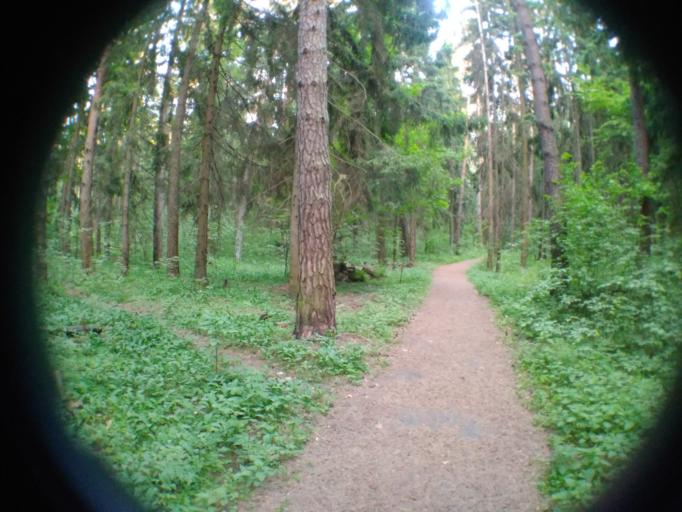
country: RU
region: Moskovskaya
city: Zhukovskiy
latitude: 55.5840
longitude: 38.1200
